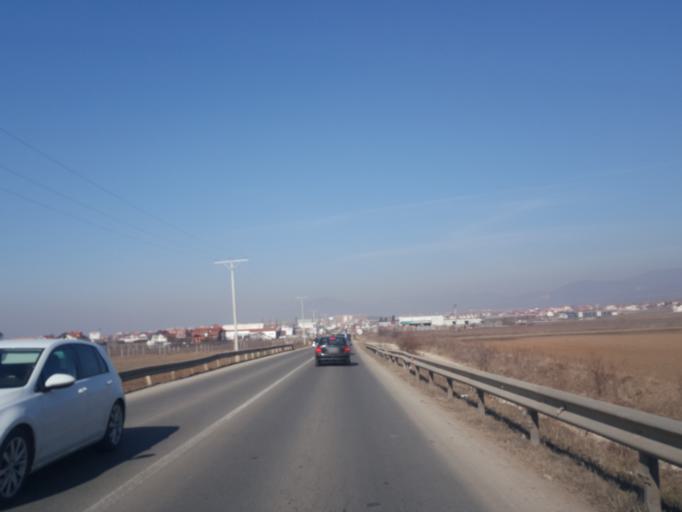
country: XK
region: Mitrovica
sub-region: Vushtrri
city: Vushtrri
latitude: 42.8031
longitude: 20.9930
